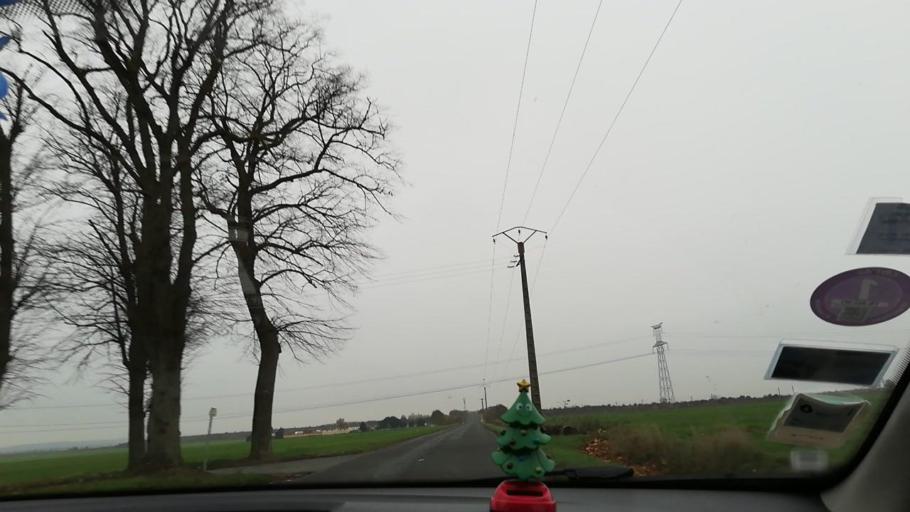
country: FR
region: Ile-de-France
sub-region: Departement de Seine-et-Marne
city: Charny
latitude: 48.9687
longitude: 2.7411
